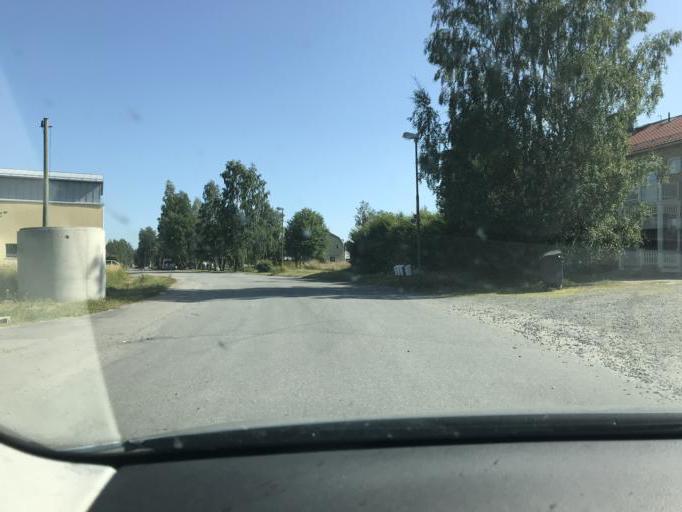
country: SE
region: Norrbotten
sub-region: Lulea Kommun
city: Gammelstad
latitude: 65.6427
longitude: 22.0168
